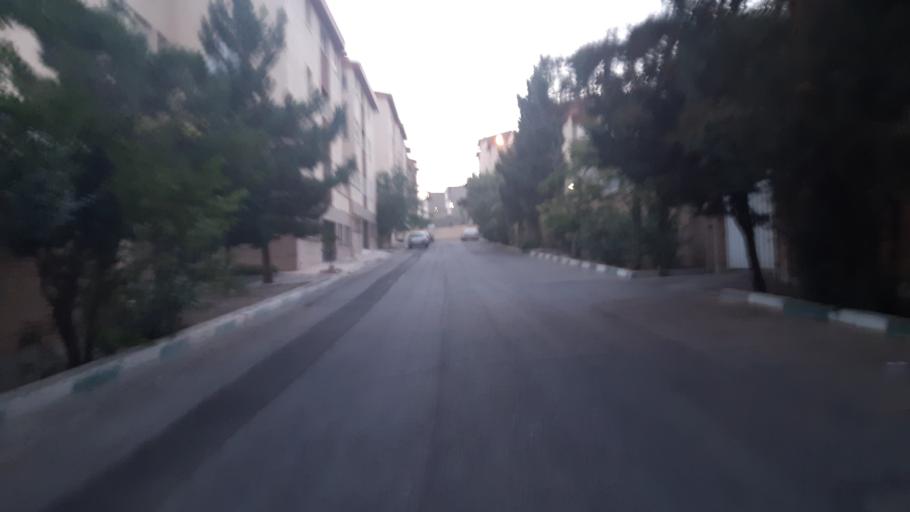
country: IR
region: Tehran
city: Shahr-e Qods
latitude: 35.7552
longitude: 51.1529
